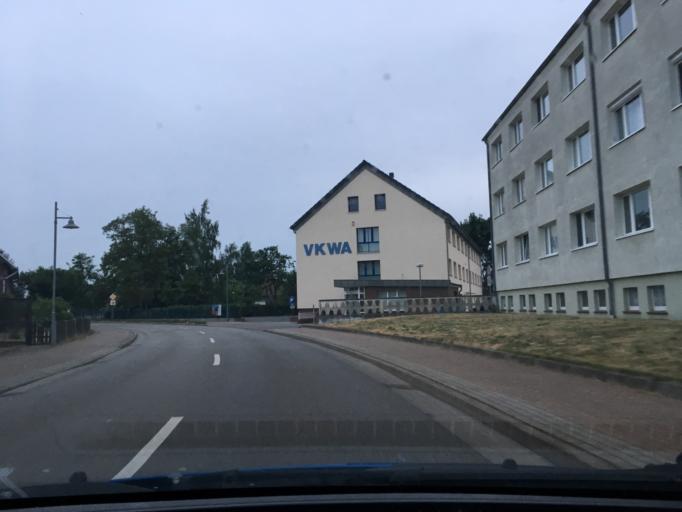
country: DE
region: Saxony-Anhalt
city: Salzwedel
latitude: 52.8584
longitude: 11.1492
